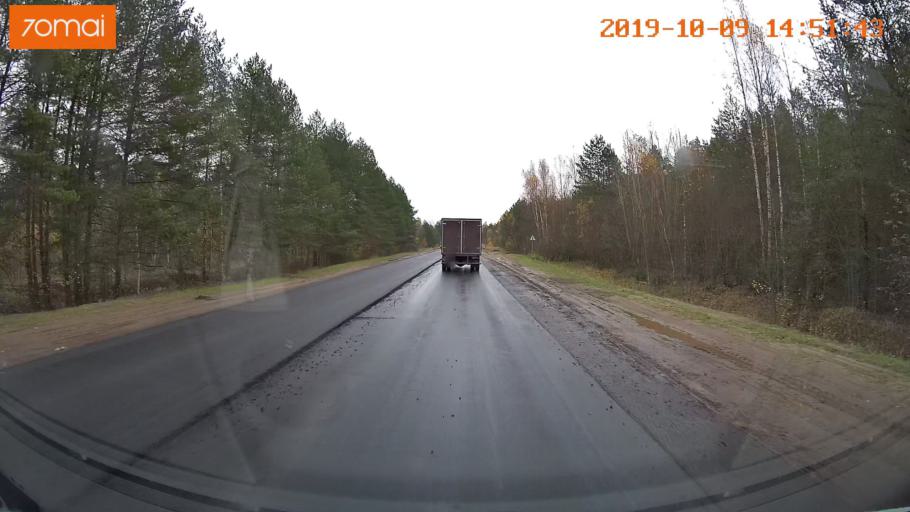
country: RU
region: Kostroma
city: Chistyye Bory
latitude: 58.3776
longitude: 41.6178
